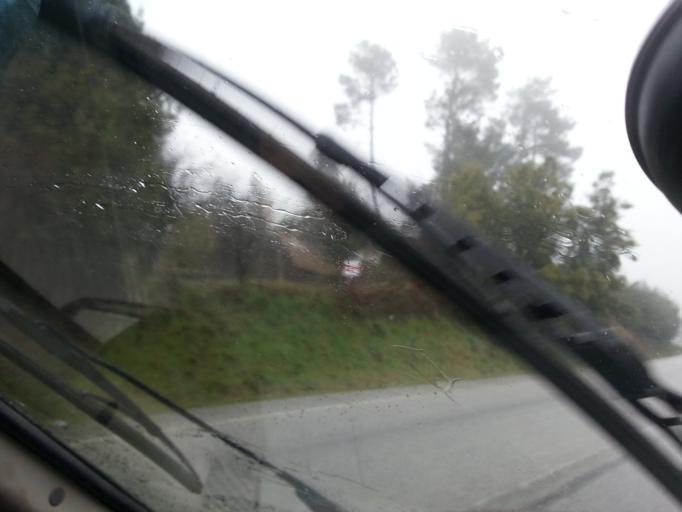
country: PT
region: Viseu
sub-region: Mangualde
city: Mangualde
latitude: 40.6076
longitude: -7.7797
